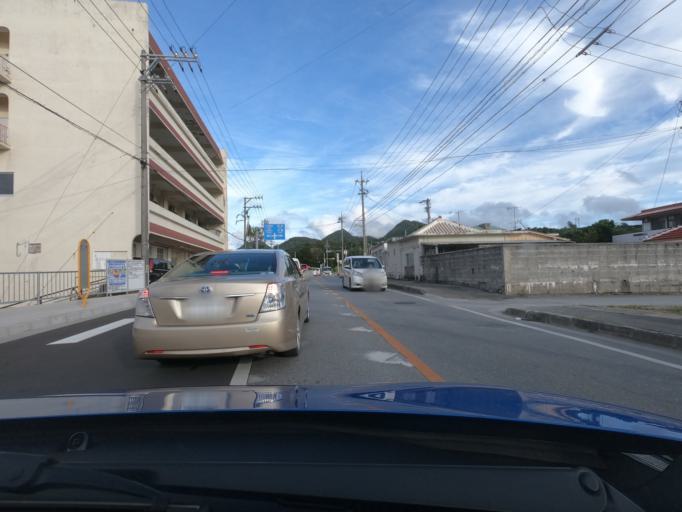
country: JP
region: Okinawa
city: Nago
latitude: 26.6778
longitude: 127.8907
